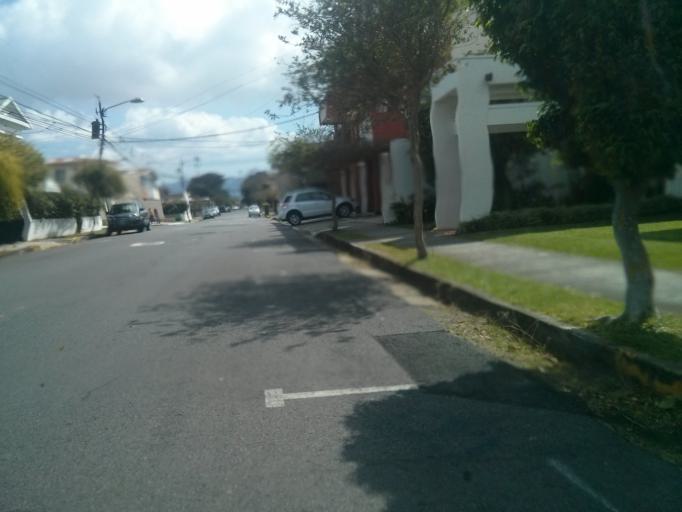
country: CR
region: San Jose
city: Calle Blancos
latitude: 9.9373
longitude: -84.0643
